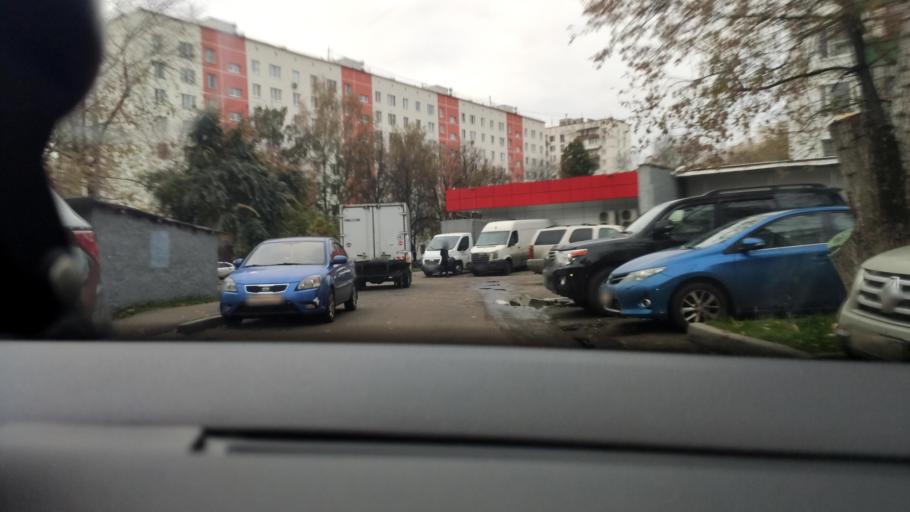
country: RU
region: Moscow
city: Novokuz'minki
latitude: 55.7144
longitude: 37.7842
